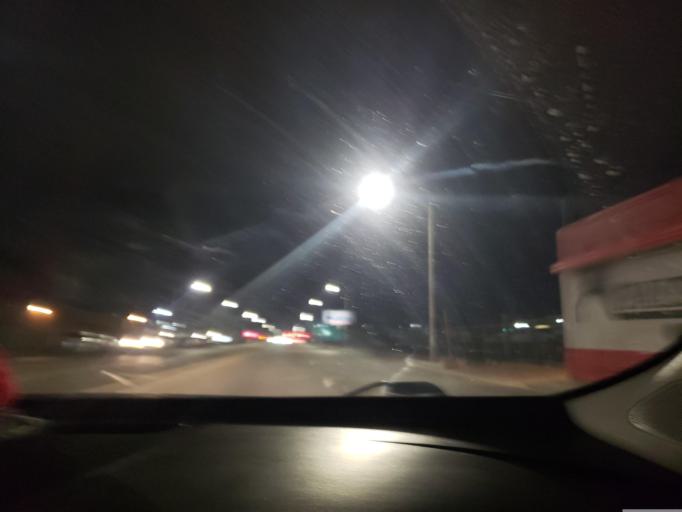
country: US
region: New Mexico
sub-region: Bernalillo County
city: Albuquerque
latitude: 35.1070
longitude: -106.6448
